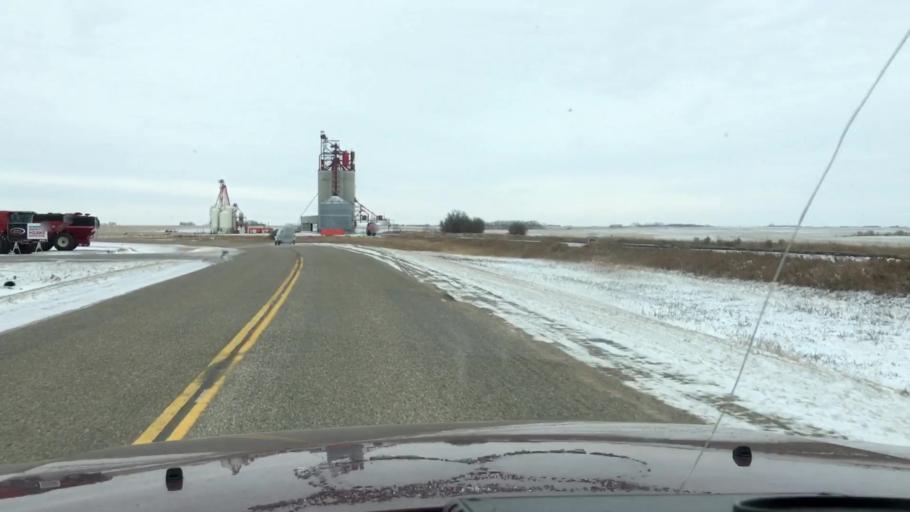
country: CA
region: Saskatchewan
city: Watrous
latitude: 51.2503
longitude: -105.9778
